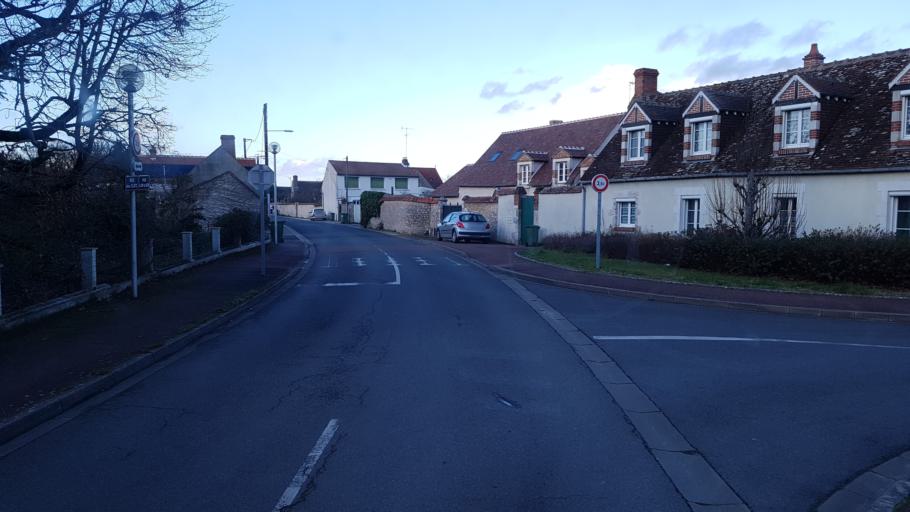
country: FR
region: Centre
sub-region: Departement du Loiret
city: Olivet
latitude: 47.8492
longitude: 1.9183
